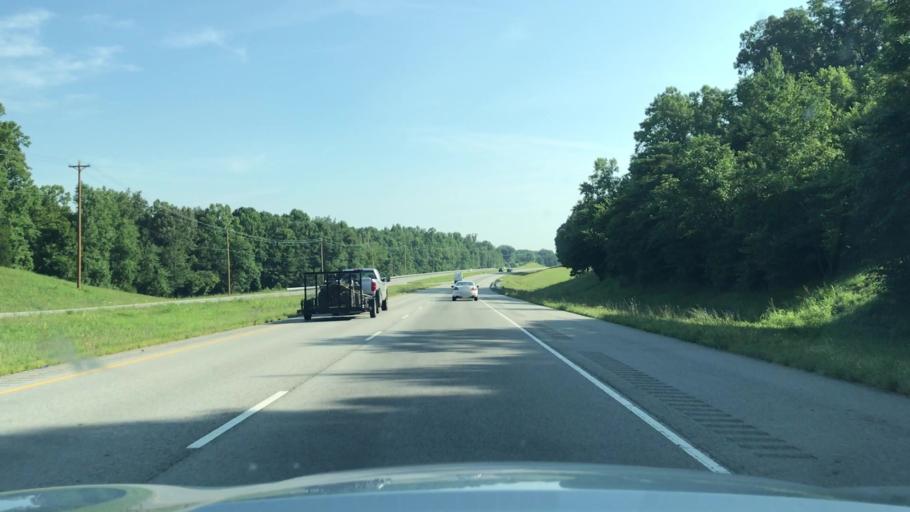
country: US
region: Tennessee
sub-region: Overton County
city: Livingston
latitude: 36.3186
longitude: -85.3627
